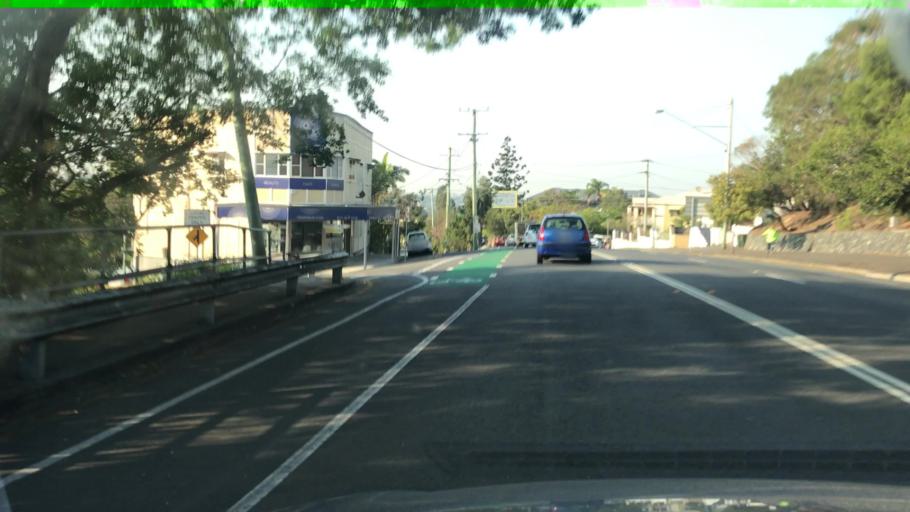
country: AU
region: Queensland
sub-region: Brisbane
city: South Brisbane
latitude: -27.4884
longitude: 153.0187
